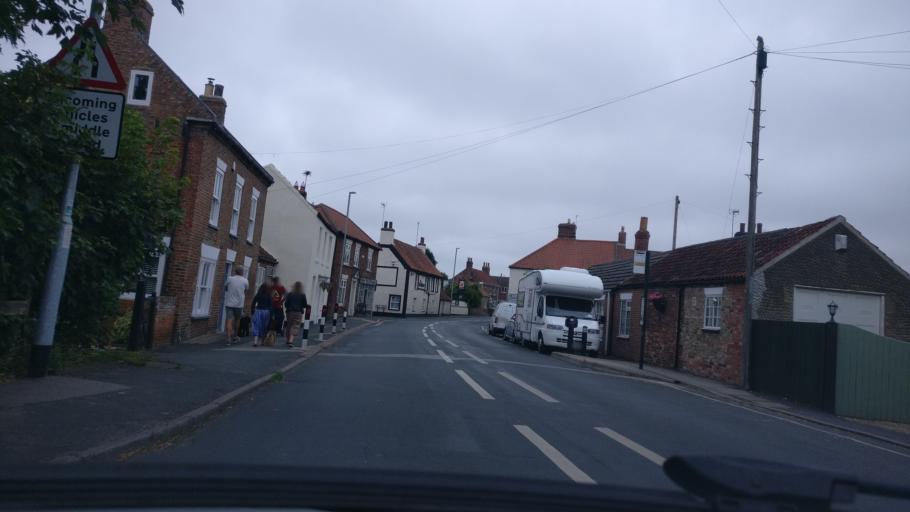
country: GB
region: England
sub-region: East Riding of Yorkshire
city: Leven
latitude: 53.8921
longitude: -0.3173
